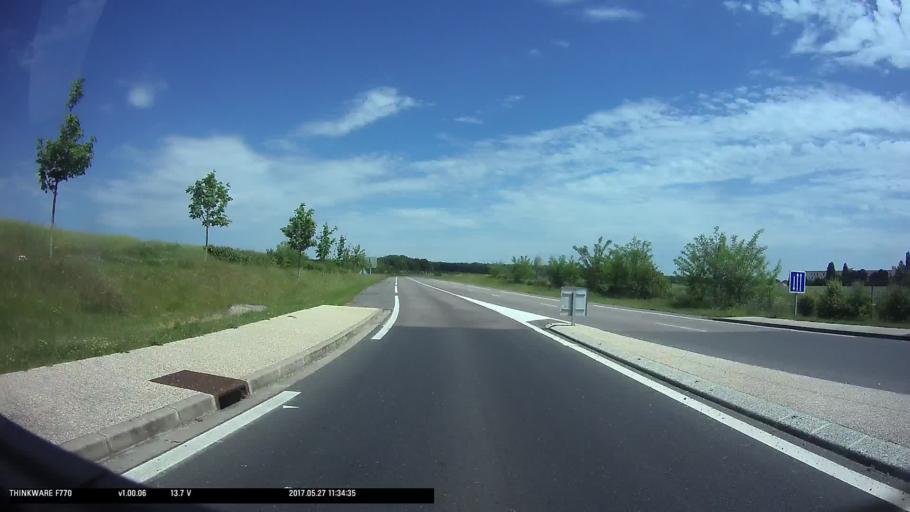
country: FR
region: Haute-Normandie
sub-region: Departement de l'Eure
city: Neaufles-Saint-Martin
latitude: 49.2806
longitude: 1.7532
